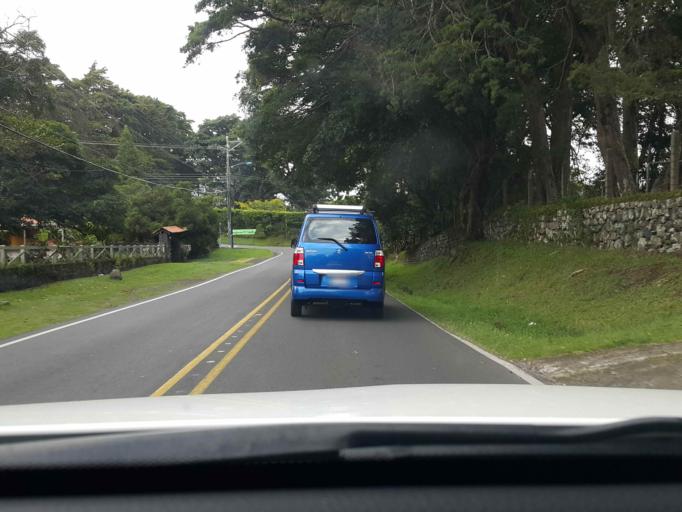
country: CR
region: Heredia
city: San Josecito
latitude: 10.0463
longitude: -84.0892
